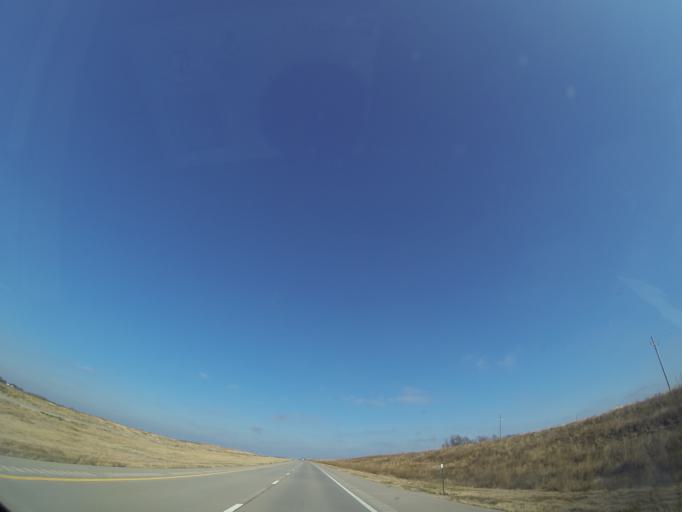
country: US
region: Kansas
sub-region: Reno County
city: Buhler
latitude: 38.1800
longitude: -97.8178
